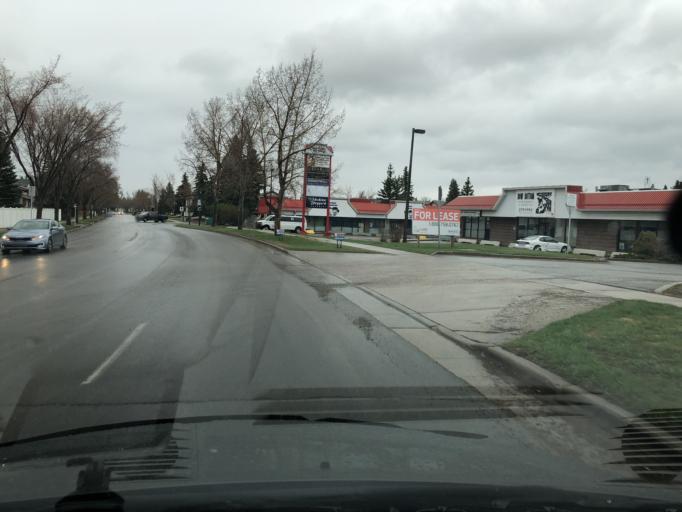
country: CA
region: Alberta
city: Calgary
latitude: 50.9292
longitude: -114.0272
